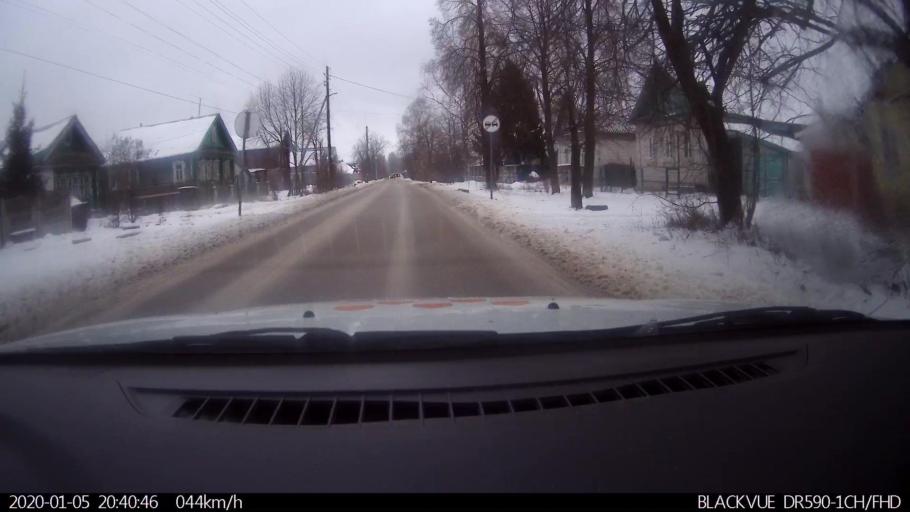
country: RU
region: Nizjnij Novgorod
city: Lukino
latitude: 56.4078
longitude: 43.7284
